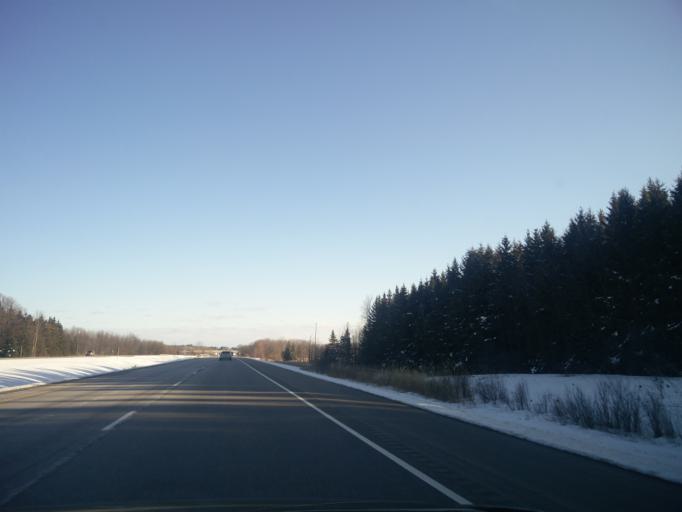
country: CA
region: Ontario
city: Prescott
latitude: 44.8556
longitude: -75.5420
